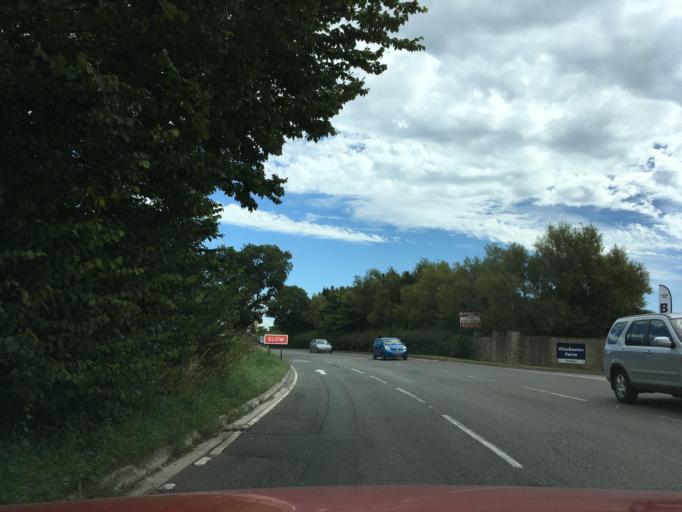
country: GB
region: England
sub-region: Somerset
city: Bradley Cross
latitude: 51.2670
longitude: -2.7680
